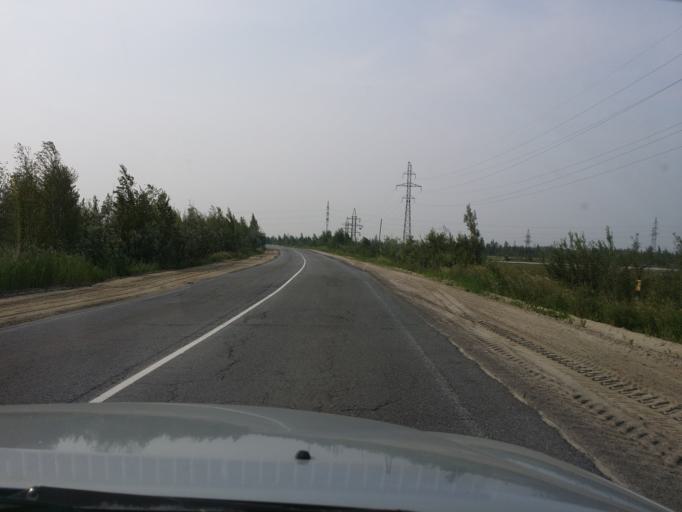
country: RU
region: Khanty-Mansiyskiy Avtonomnyy Okrug
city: Nizhnevartovsk
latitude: 61.0952
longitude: 76.6459
